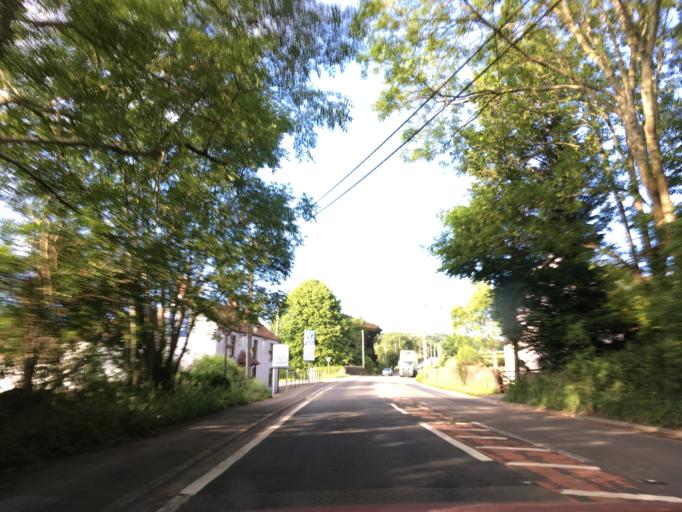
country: GB
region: England
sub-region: North Somerset
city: Churchill
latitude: 51.3214
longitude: -2.8071
